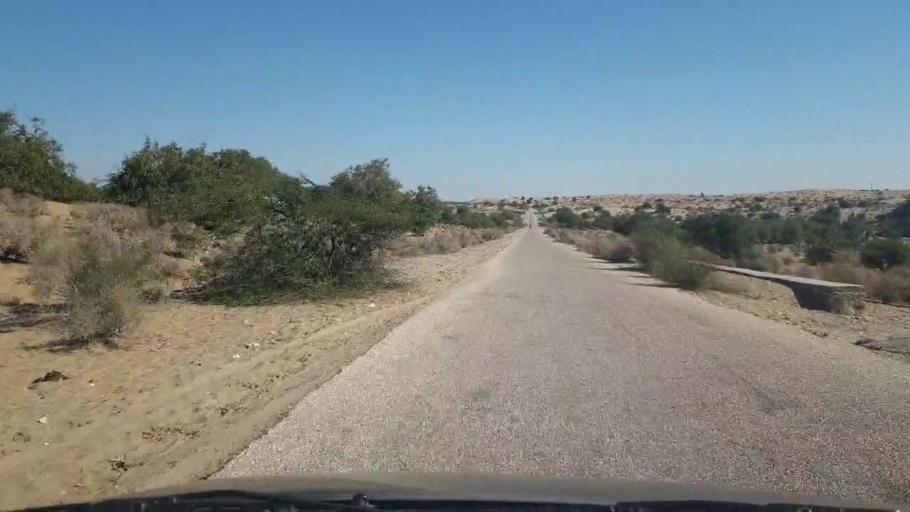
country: PK
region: Sindh
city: Bozdar
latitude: 27.0066
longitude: 68.9004
